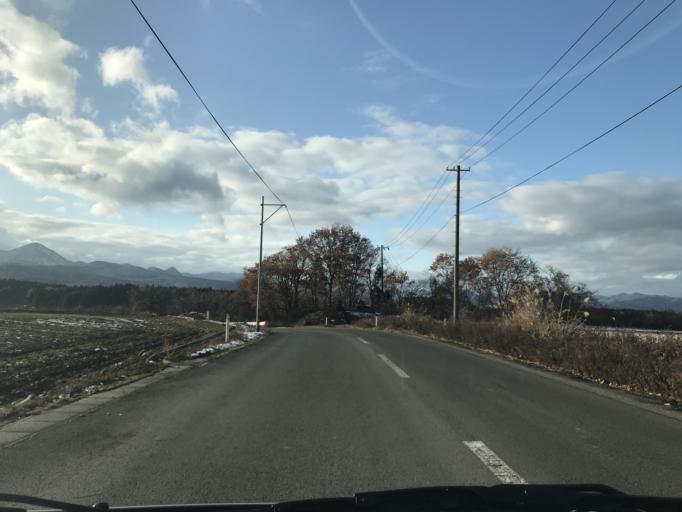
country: JP
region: Iwate
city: Kitakami
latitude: 39.2556
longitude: 141.0307
